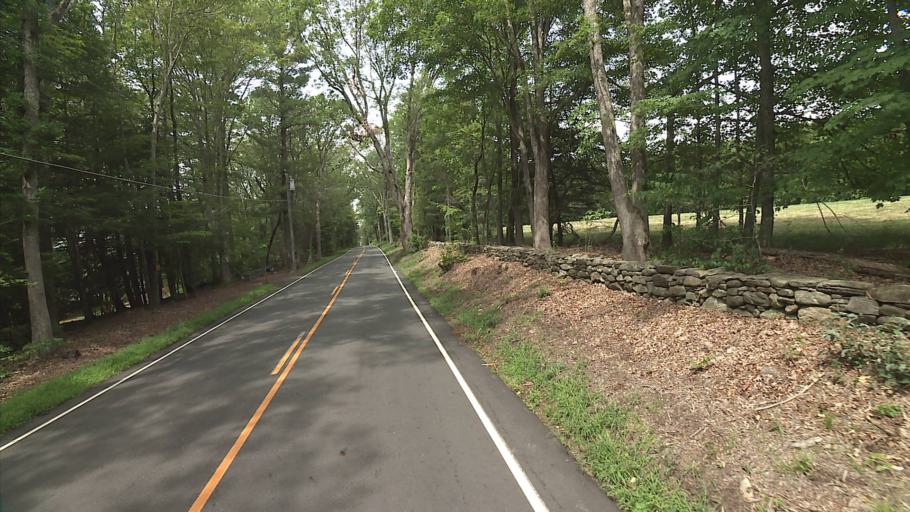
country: US
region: Massachusetts
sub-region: Hampden County
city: Holland
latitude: 41.9750
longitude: -72.1134
